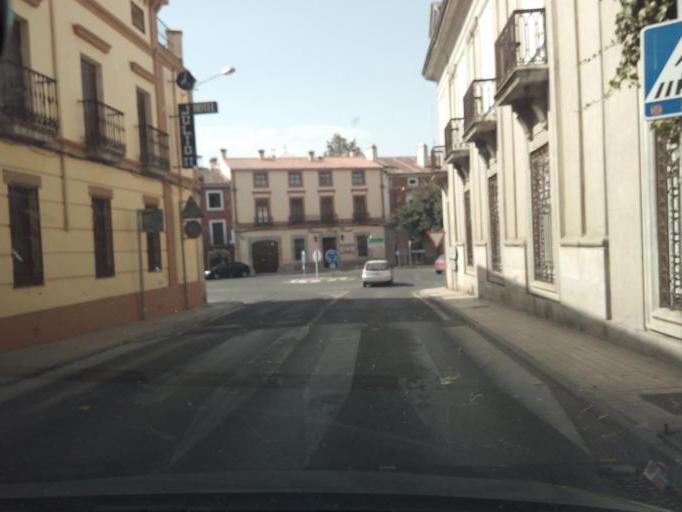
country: ES
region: Extremadura
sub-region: Provincia de Caceres
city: Trujillo
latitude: 39.4588
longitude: -5.8767
